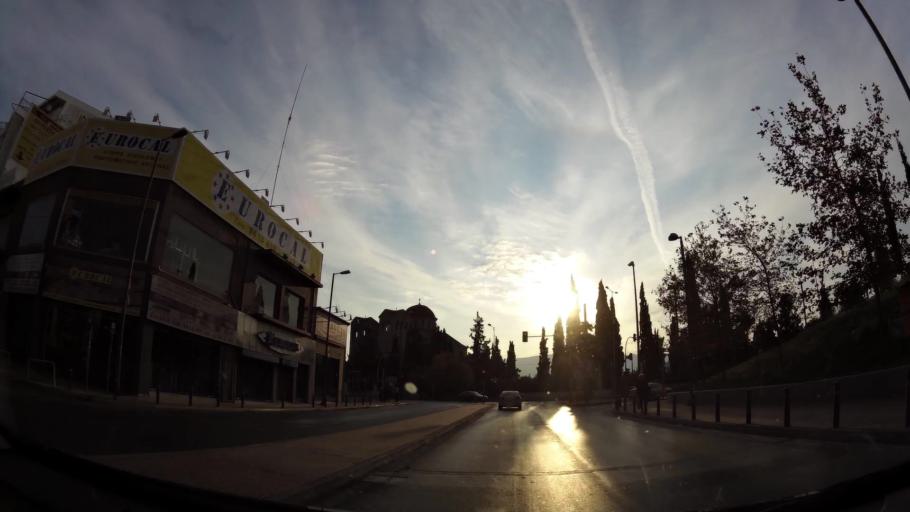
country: GR
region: Attica
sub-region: Nomarchia Athinas
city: Athens
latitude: 37.9792
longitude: 23.7160
